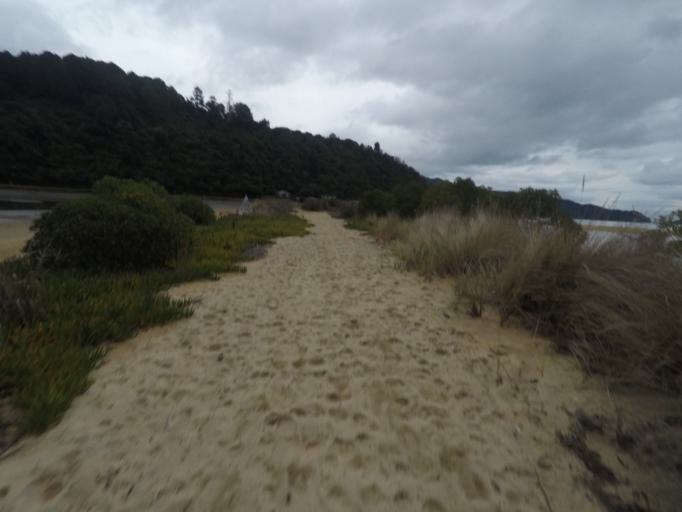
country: NZ
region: Tasman
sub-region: Tasman District
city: Motueka
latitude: -41.0111
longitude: 173.0073
